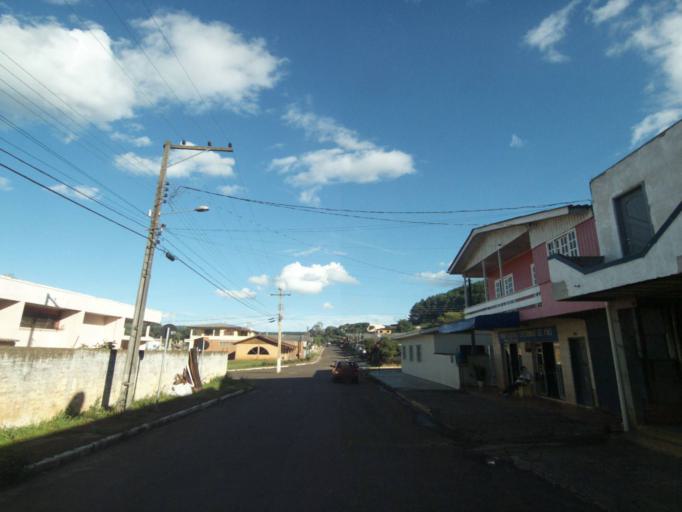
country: BR
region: Parana
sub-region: Uniao Da Vitoria
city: Uniao da Vitoria
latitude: -26.1665
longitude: -51.5356
